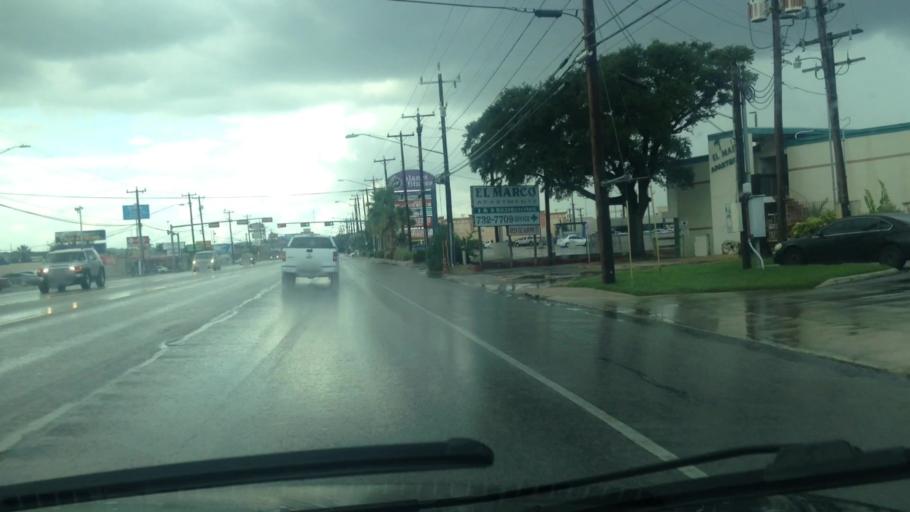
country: US
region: Texas
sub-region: Bexar County
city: Balcones Heights
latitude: 29.4867
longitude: -98.5481
